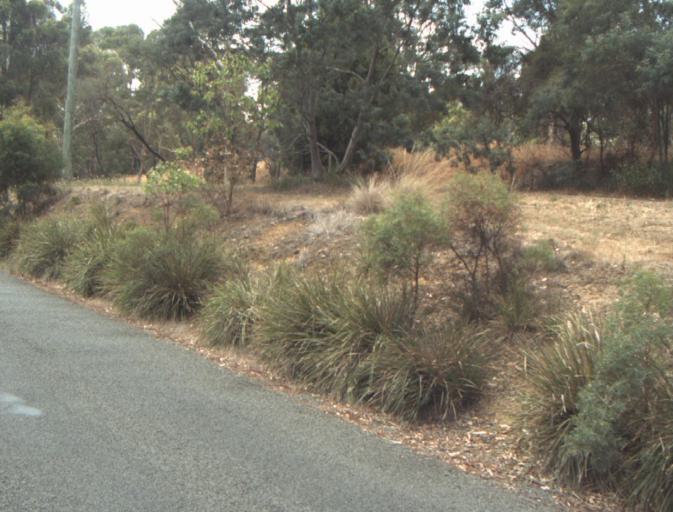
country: AU
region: Tasmania
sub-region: Launceston
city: East Launceston
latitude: -41.4663
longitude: 147.1676
